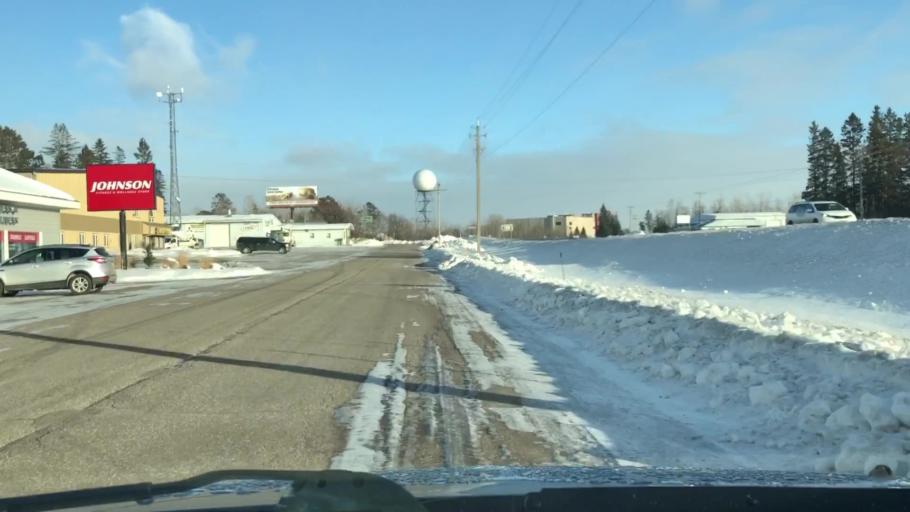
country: US
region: Minnesota
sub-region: Saint Louis County
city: Hermantown
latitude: 46.8370
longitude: -92.2153
